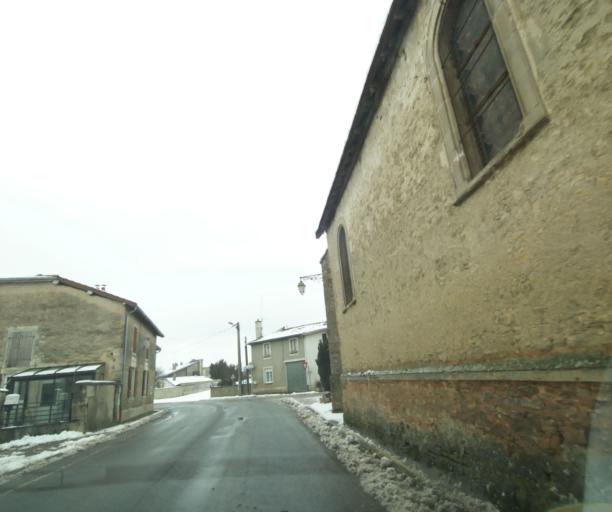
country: FR
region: Champagne-Ardenne
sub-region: Departement de la Haute-Marne
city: Montier-en-Der
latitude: 48.4204
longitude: 4.8190
